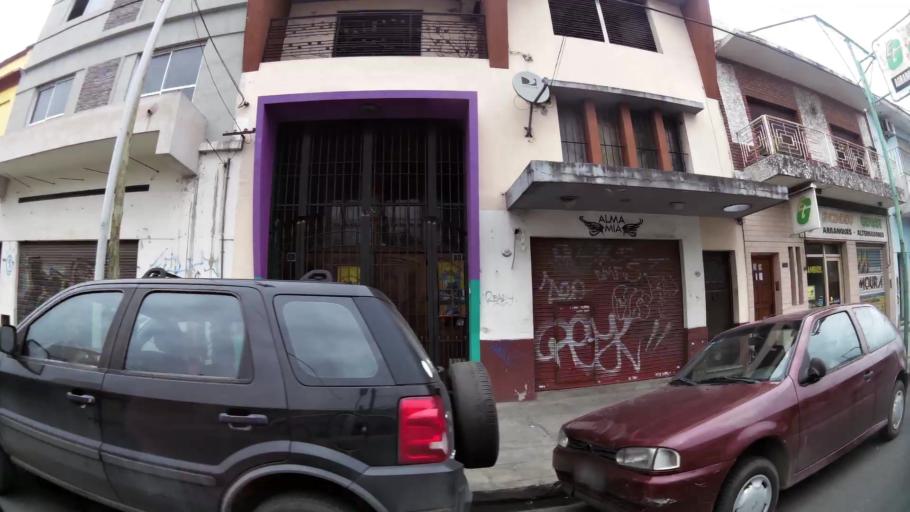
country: AR
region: Buenos Aires
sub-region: Partido de Lanus
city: Lanus
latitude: -34.6875
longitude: -58.3771
